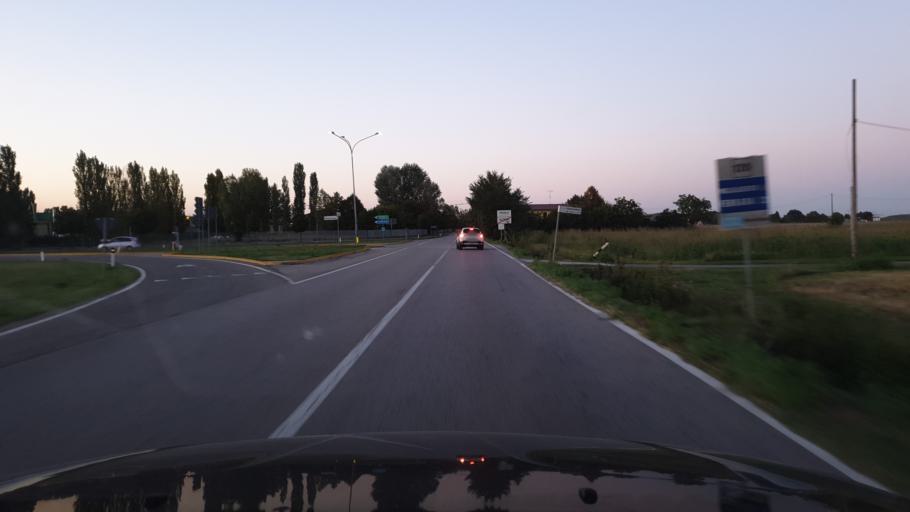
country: IT
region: Emilia-Romagna
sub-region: Provincia di Bologna
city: Altedo
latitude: 44.6819
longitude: 11.4971
